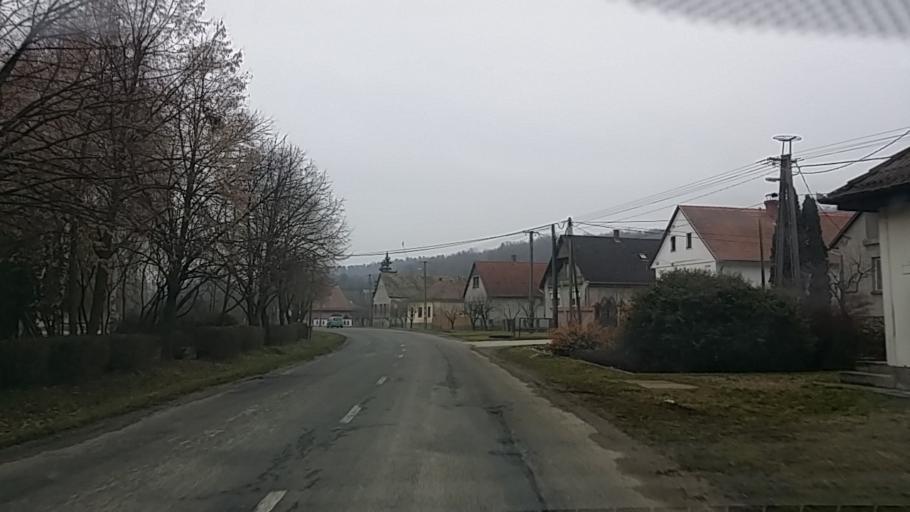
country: HU
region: Baranya
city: Lanycsok
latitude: 46.0459
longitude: 18.6023
